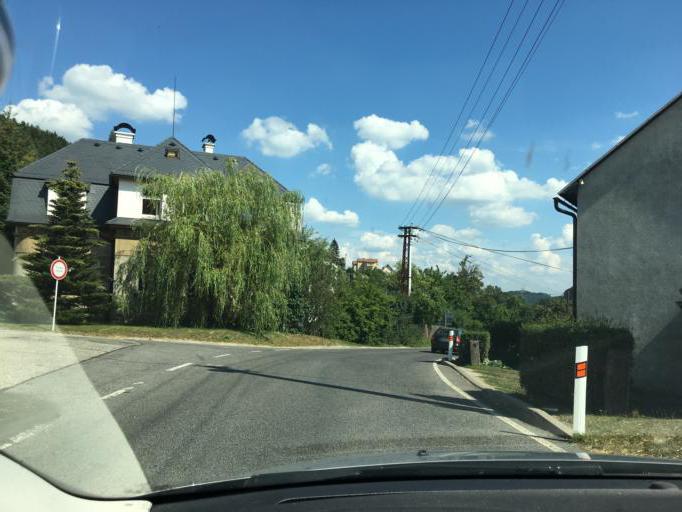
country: CZ
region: Liberecky
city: Mala Skala
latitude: 50.6518
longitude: 15.1565
